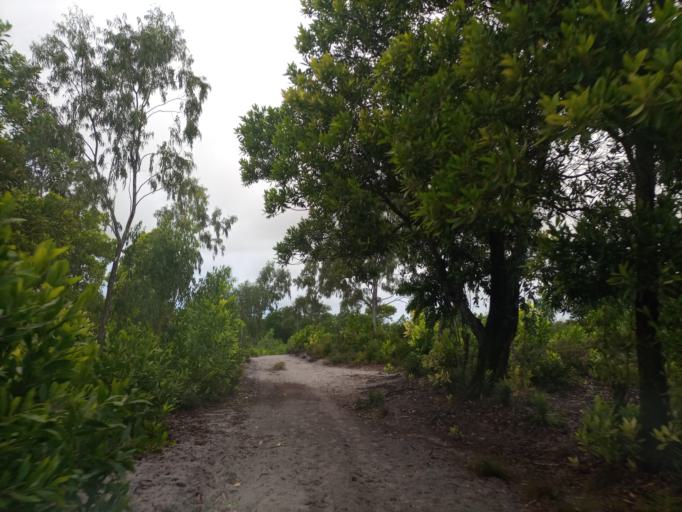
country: MG
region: Anosy
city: Fort Dauphin
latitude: -24.6476
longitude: 47.2048
